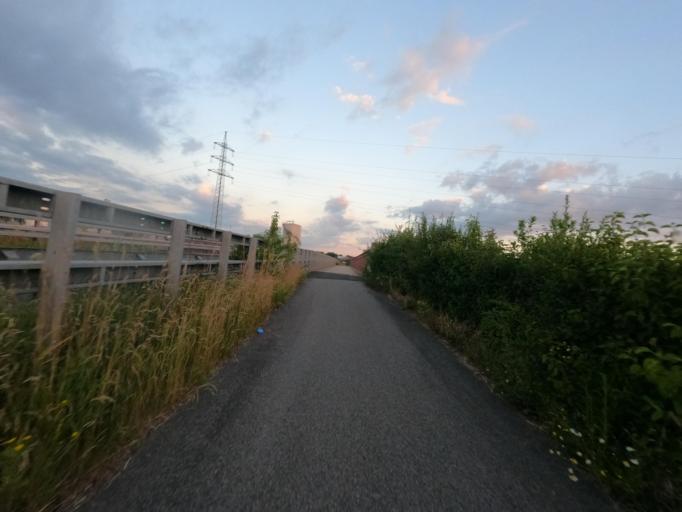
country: DE
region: North Rhine-Westphalia
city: Baesweiler
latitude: 50.9227
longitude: 6.1533
